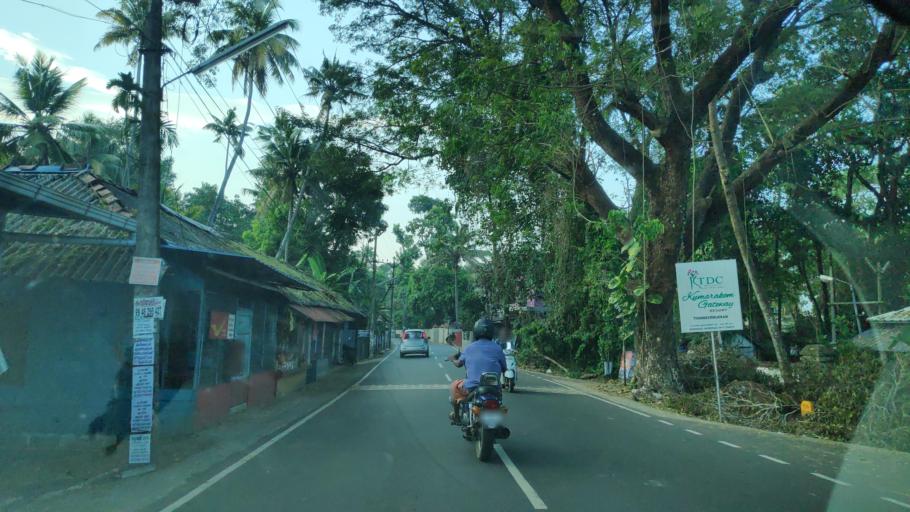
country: IN
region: Kerala
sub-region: Alappuzha
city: Shertallai
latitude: 9.6771
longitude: 76.3927
